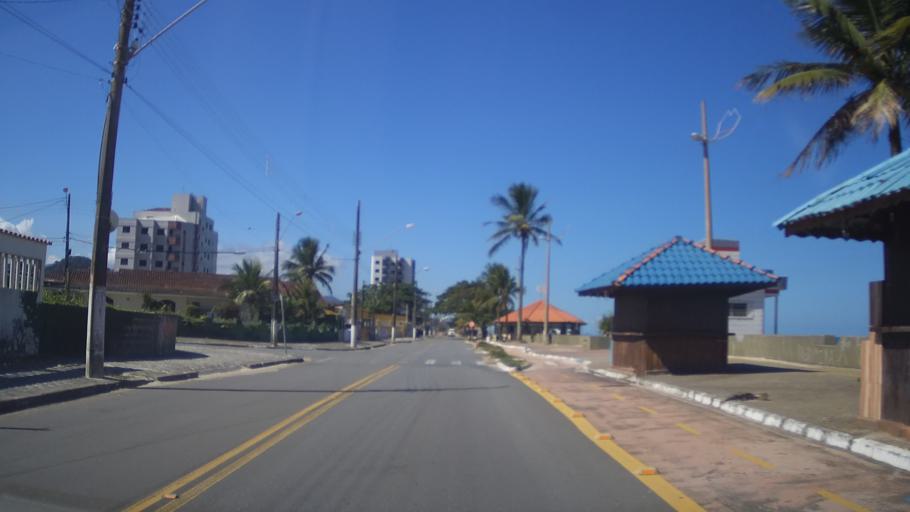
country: BR
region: Sao Paulo
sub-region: Mongagua
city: Mongagua
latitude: -24.1301
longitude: -46.6866
